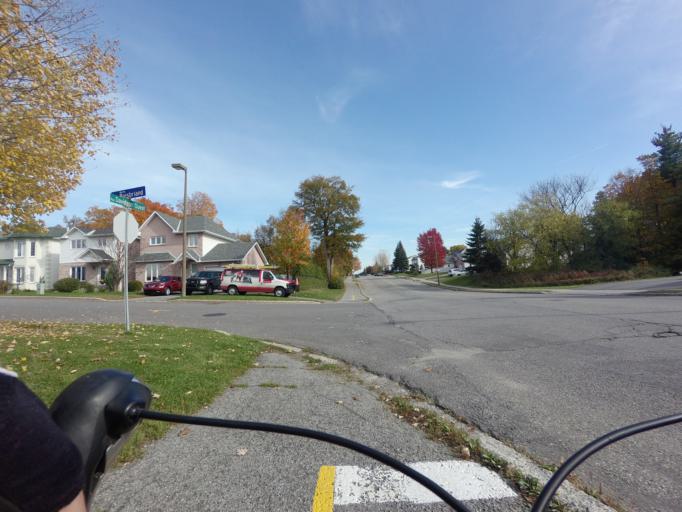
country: CA
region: Quebec
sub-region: Outaouais
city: Gatineau
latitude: 45.5072
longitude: -75.6580
